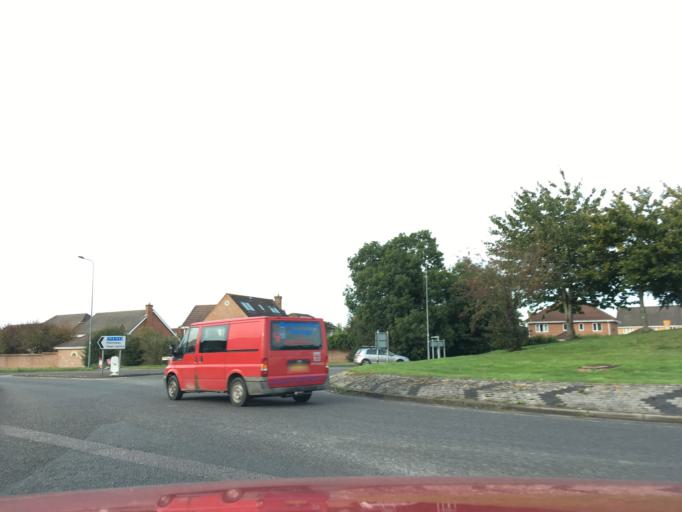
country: GB
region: England
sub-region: South Gloucestershire
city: Stoke Gifford
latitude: 51.5276
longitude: -2.5384
